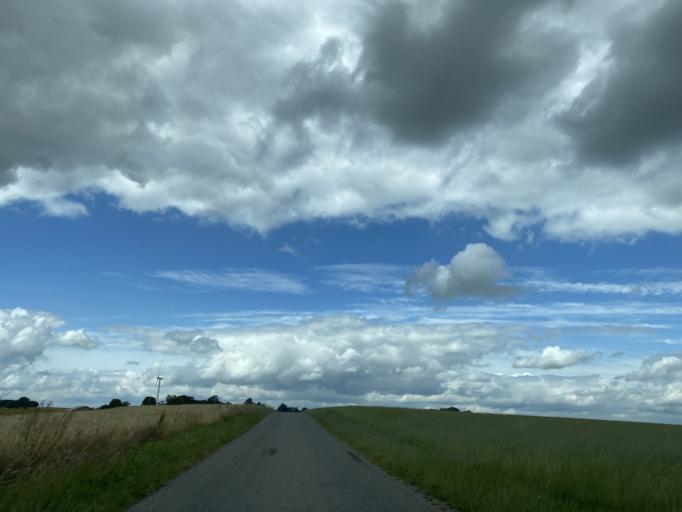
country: DK
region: Central Jutland
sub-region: Silkeborg Kommune
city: Svejbaek
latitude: 56.2376
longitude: 9.6441
